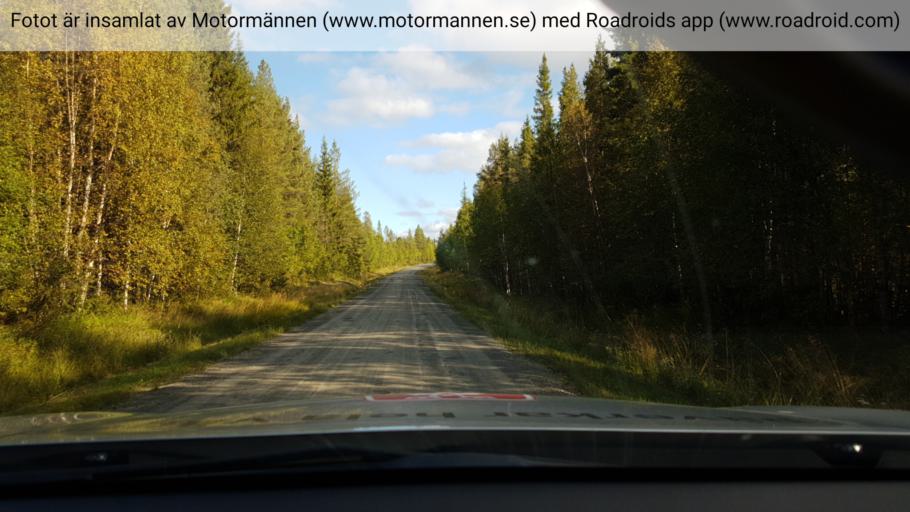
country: SE
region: Vaesterbotten
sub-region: Sorsele Kommun
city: Sorsele
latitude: 65.4626
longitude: 17.6857
